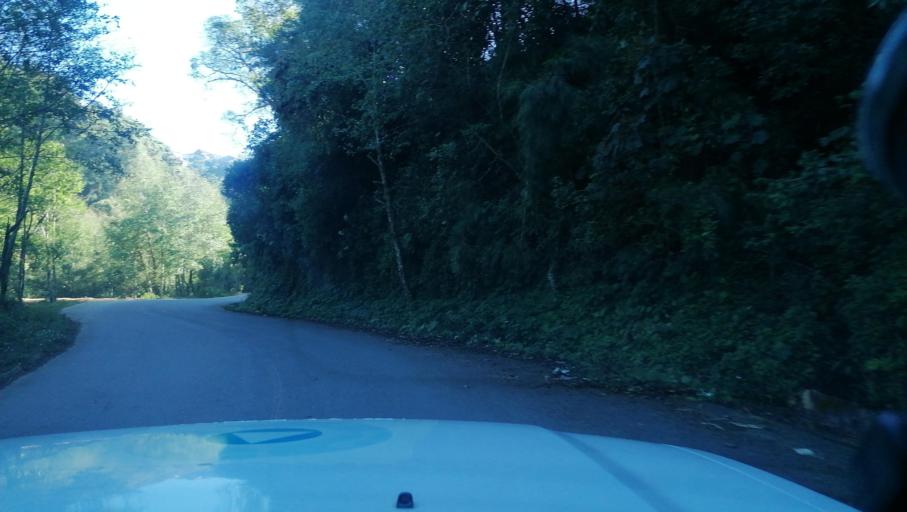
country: MX
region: Chiapas
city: Motozintla de Mendoza
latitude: 15.2568
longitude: -92.2149
